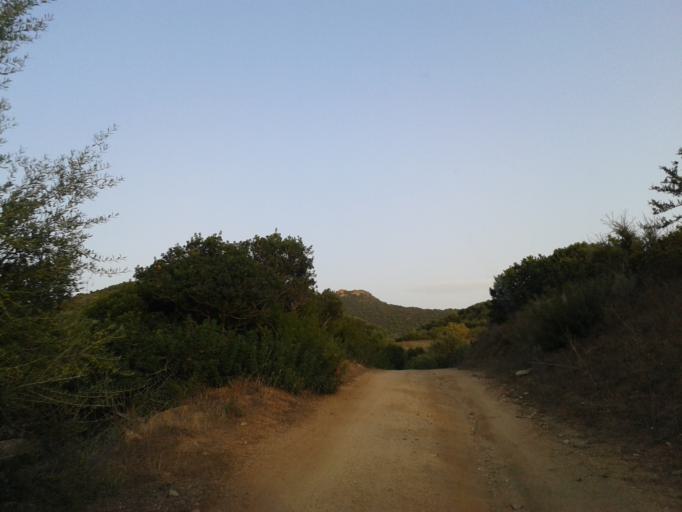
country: IT
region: Sardinia
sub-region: Provincia di Cagliari
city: Villasimius
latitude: 39.1381
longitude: 9.4995
